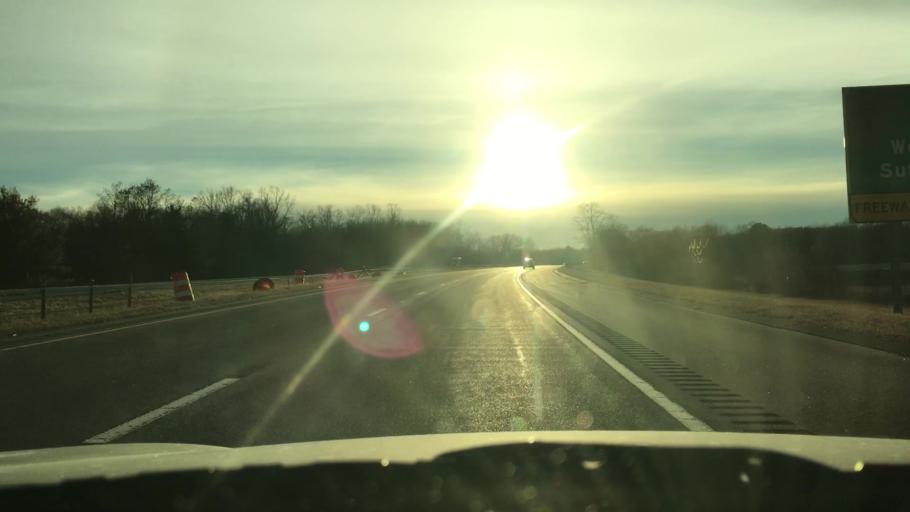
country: US
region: Massachusetts
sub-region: Hampden County
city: Agawam
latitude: 42.0595
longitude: -72.6622
